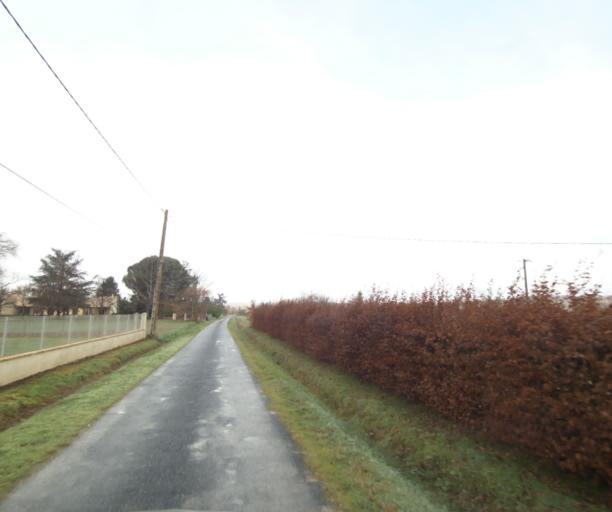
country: FR
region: Midi-Pyrenees
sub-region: Departement de la Haute-Garonne
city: Villemur-sur-Tarn
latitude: 43.8693
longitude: 1.4812
